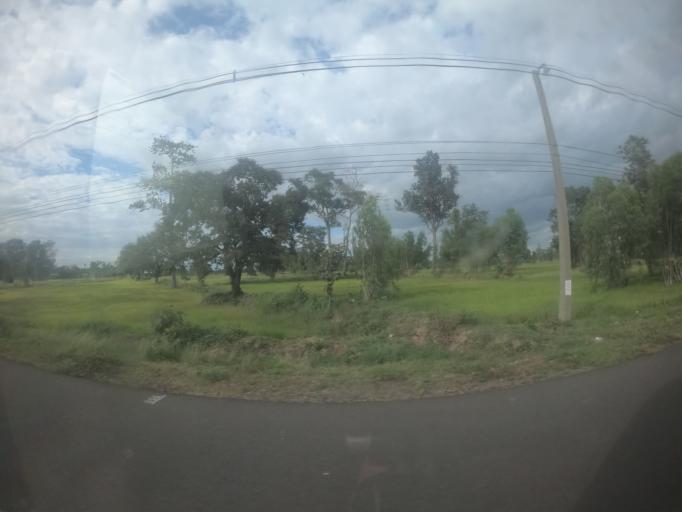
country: TH
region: Surin
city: Prasat
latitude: 14.5782
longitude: 103.4799
